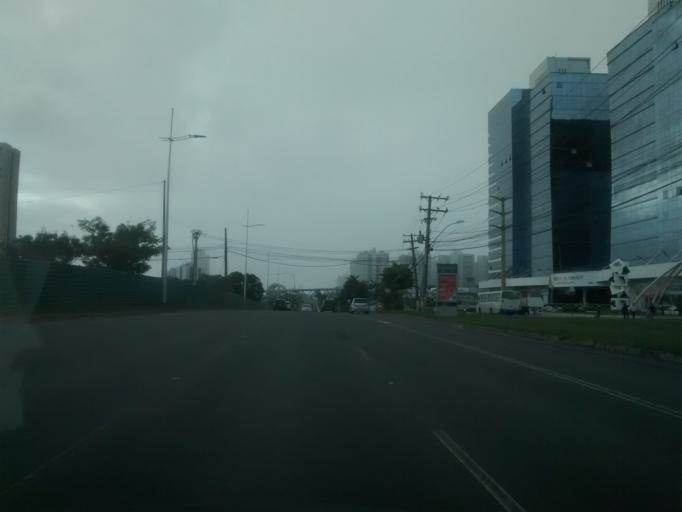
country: BR
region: Bahia
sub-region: Lauro De Freitas
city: Lauro de Freitas
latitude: -12.9397
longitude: -38.4143
